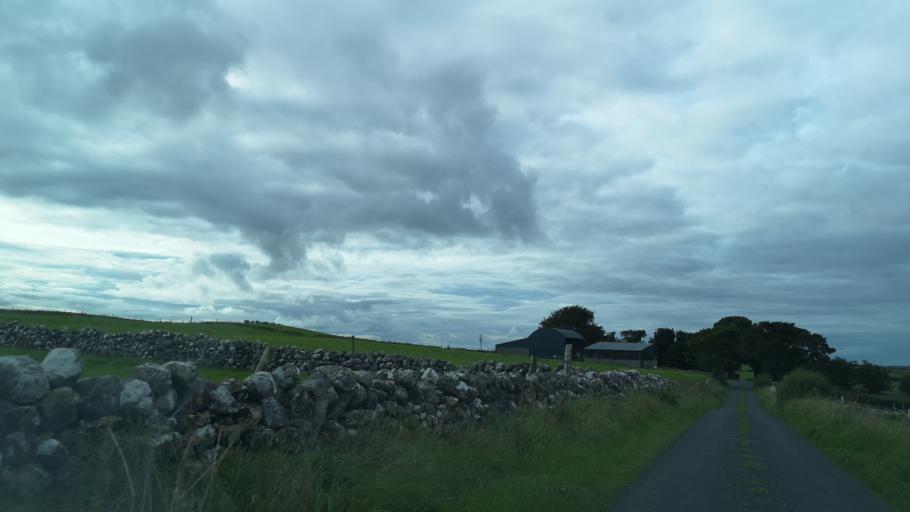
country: IE
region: Connaught
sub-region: County Galway
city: Ballinasloe
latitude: 53.3723
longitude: -8.1655
